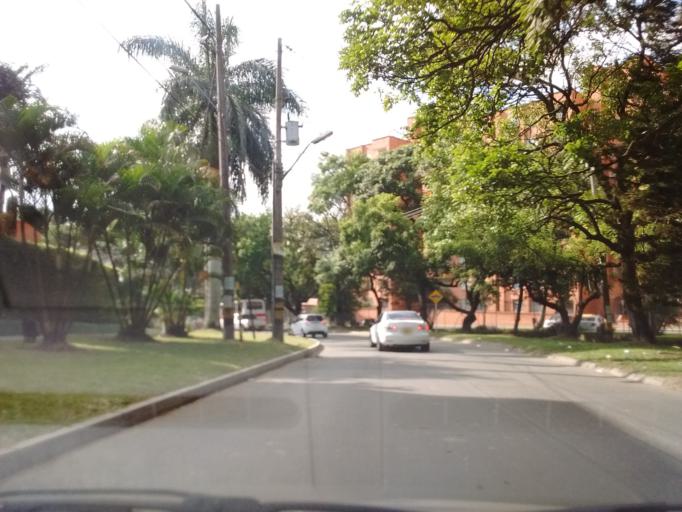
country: CO
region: Antioquia
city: Itagui
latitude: 6.2297
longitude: -75.6047
